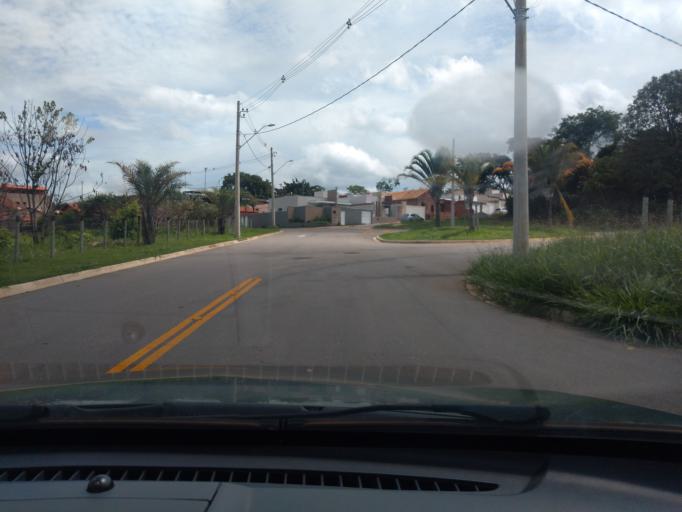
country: BR
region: Minas Gerais
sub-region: Tres Coracoes
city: Tres Coracoes
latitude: -21.6792
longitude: -45.2744
